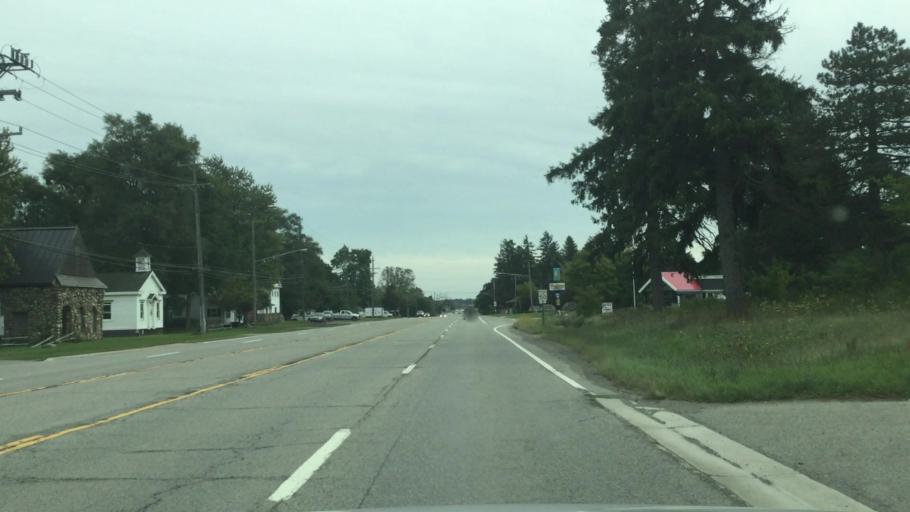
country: US
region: Michigan
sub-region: Oakland County
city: Clarkston
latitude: 42.7493
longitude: -83.4736
